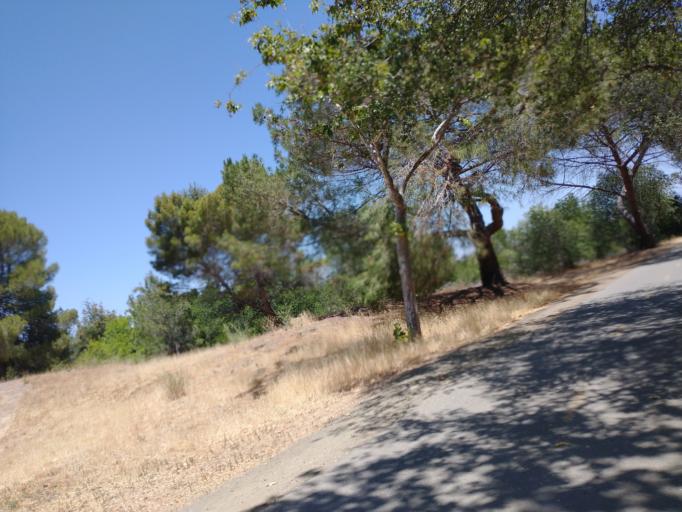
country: US
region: California
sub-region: Santa Clara County
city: Cambrian Park
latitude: 37.2622
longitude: -121.9545
